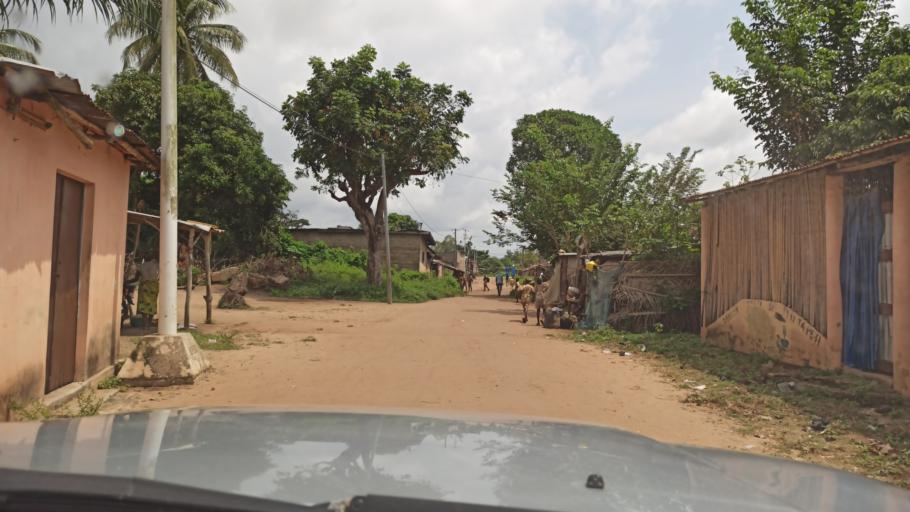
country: BJ
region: Queme
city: Porto-Novo
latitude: 6.4677
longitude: 2.6284
